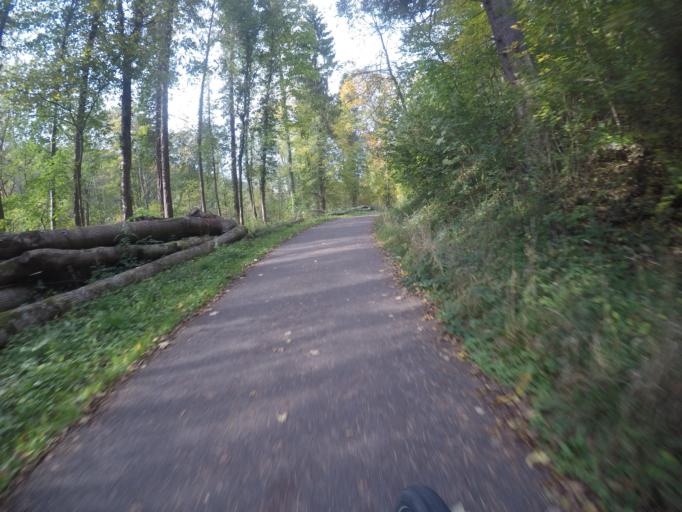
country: DE
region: Baden-Wuerttemberg
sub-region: Tuebingen Region
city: Tuebingen
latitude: 48.5425
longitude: 9.0769
